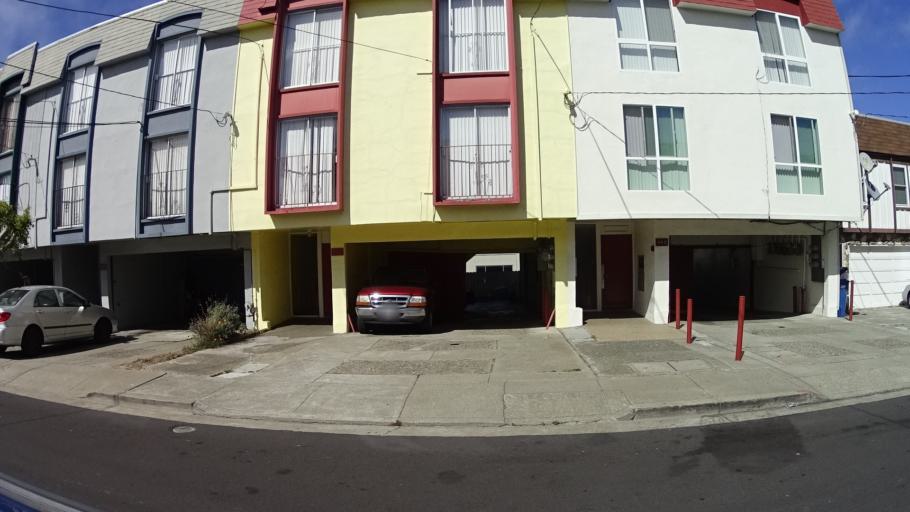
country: US
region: California
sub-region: San Mateo County
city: Broadmoor
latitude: 37.6911
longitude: -122.4753
